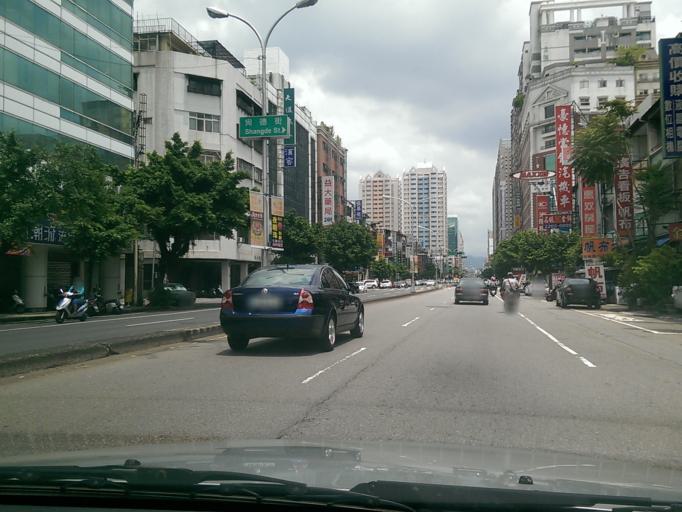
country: TW
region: Taiwan
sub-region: Taichung City
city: Taichung
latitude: 24.1632
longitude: 120.6772
